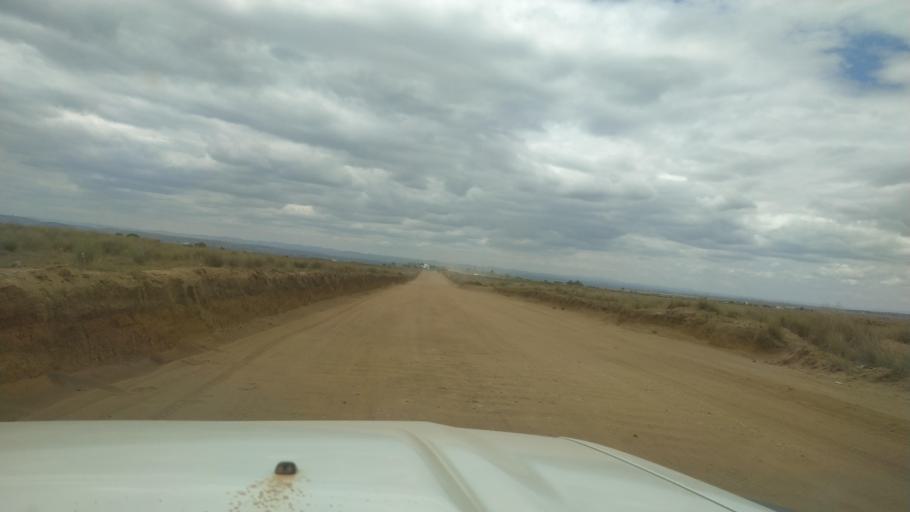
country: MG
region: Alaotra Mangoro
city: Ambatondrazaka
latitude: -17.9102
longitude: 48.2642
